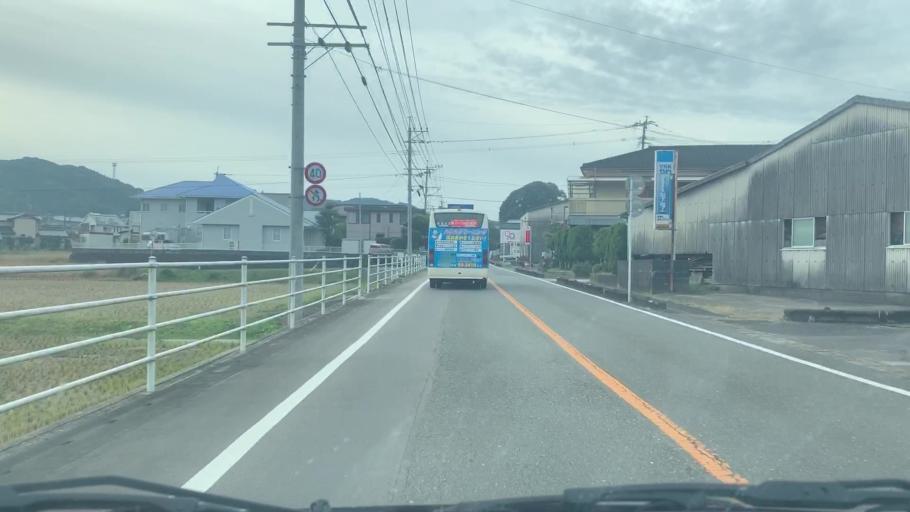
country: JP
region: Saga Prefecture
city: Ureshinomachi-shimojuku
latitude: 33.1234
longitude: 130.0026
